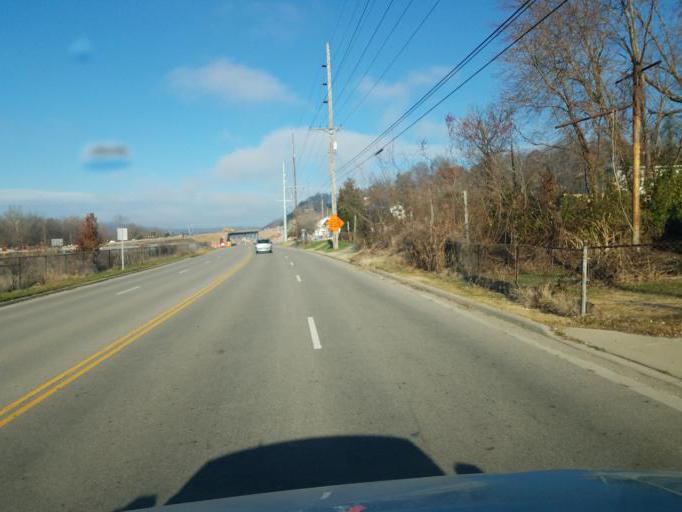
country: US
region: Ohio
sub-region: Scioto County
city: Sciotodale
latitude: 38.7439
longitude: -82.8679
